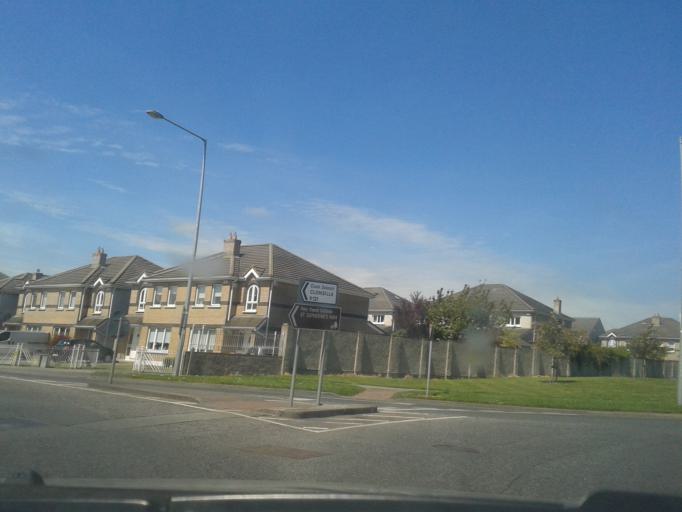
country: IE
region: Leinster
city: Hartstown
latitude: 53.3826
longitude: -6.4036
